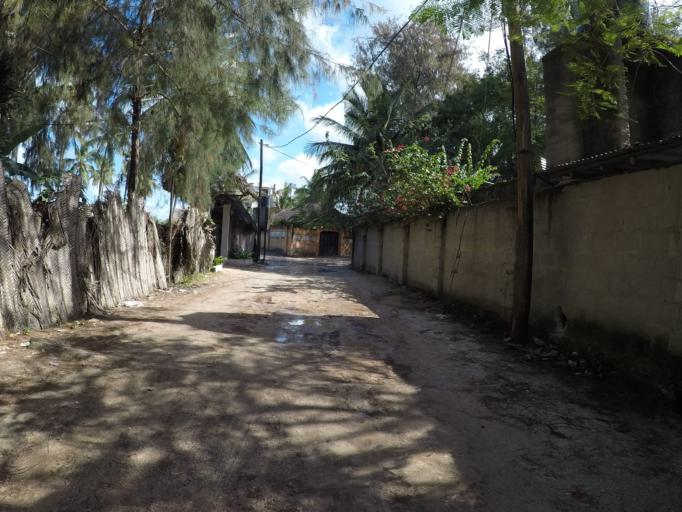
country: TZ
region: Zanzibar North
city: Nungwi
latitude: -5.7260
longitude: 39.2940
